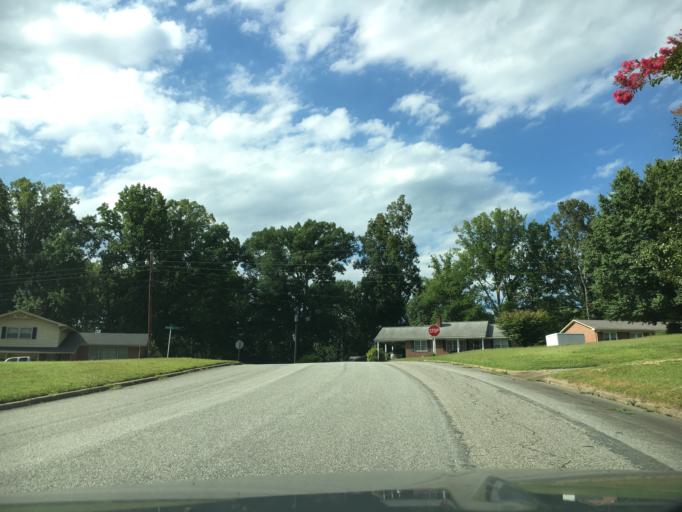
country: US
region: Virginia
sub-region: Halifax County
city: South Boston
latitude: 36.7118
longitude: -78.9095
